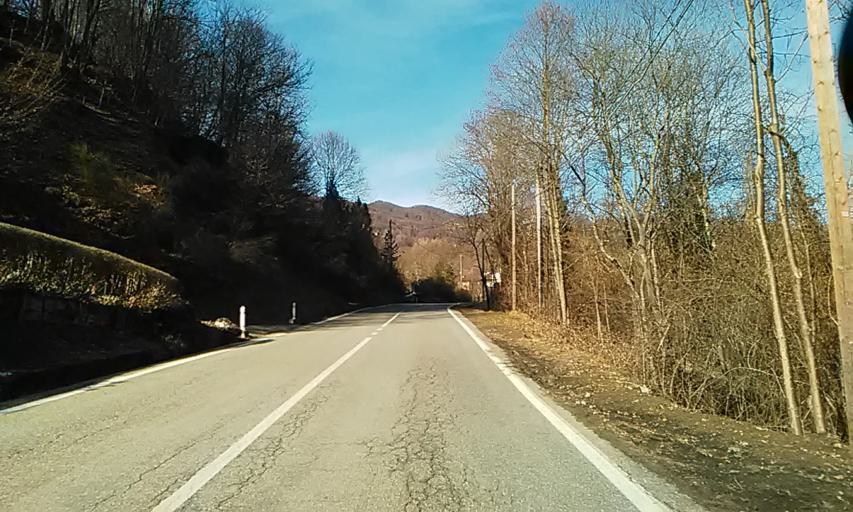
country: IT
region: Piedmont
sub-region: Provincia di Vercelli
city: Cellio
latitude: 45.7387
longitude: 8.3043
